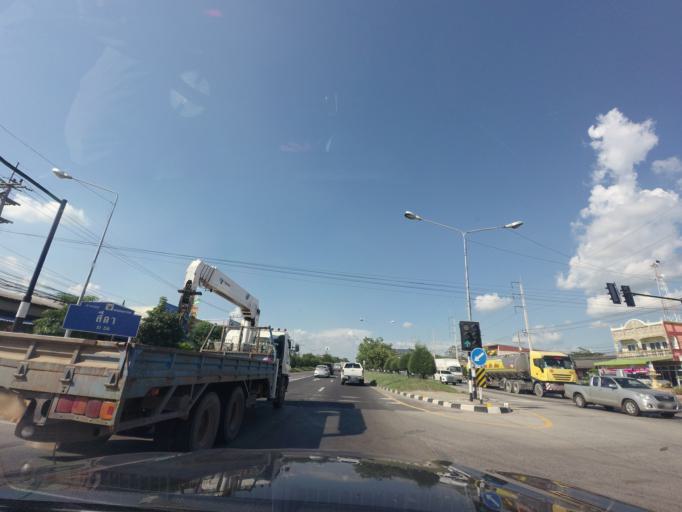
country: TH
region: Nakhon Ratchasima
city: Sida
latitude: 15.5473
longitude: 102.5479
